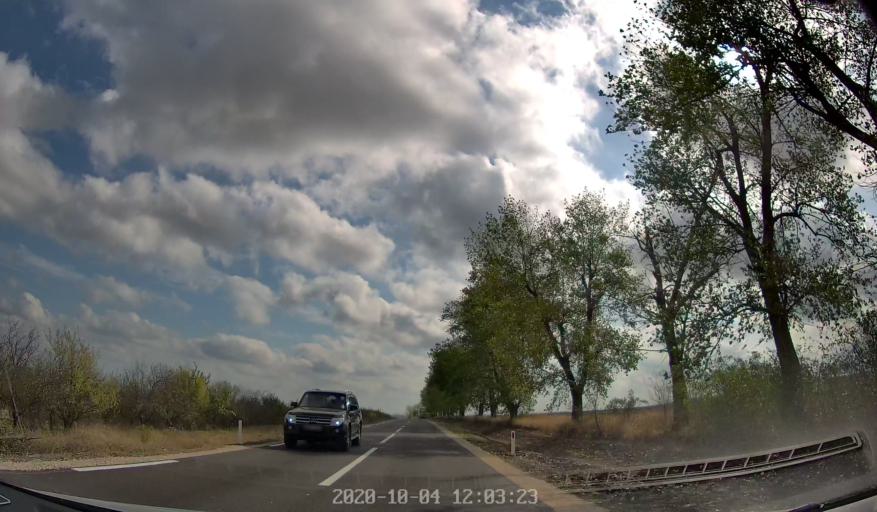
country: MD
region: Rezina
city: Saharna
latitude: 47.6123
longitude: 28.9258
